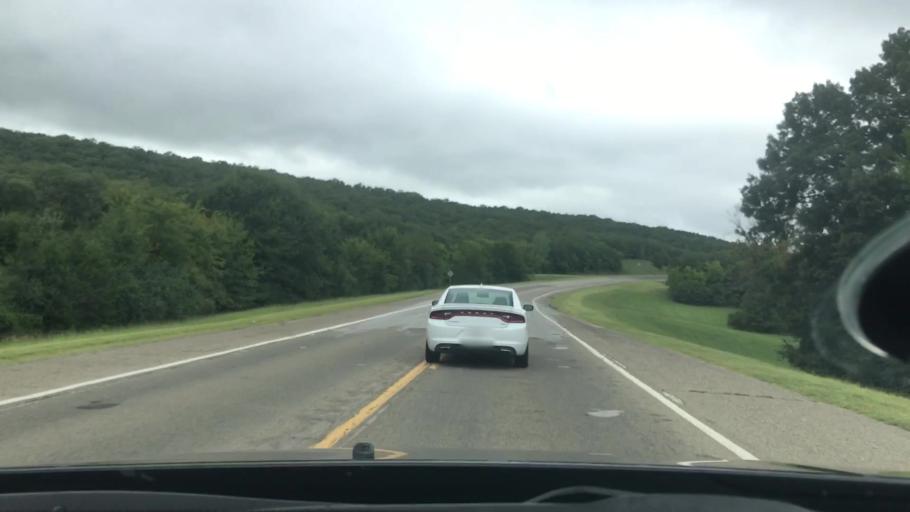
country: US
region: Oklahoma
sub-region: Sequoyah County
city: Vian
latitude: 35.5157
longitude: -94.9711
